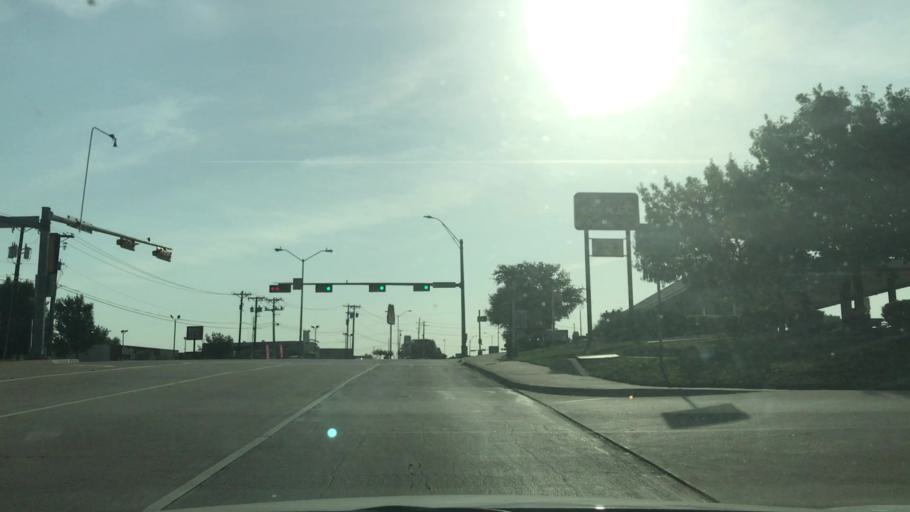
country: US
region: Texas
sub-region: Tarrant County
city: Euless
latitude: 32.7851
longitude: -97.0630
